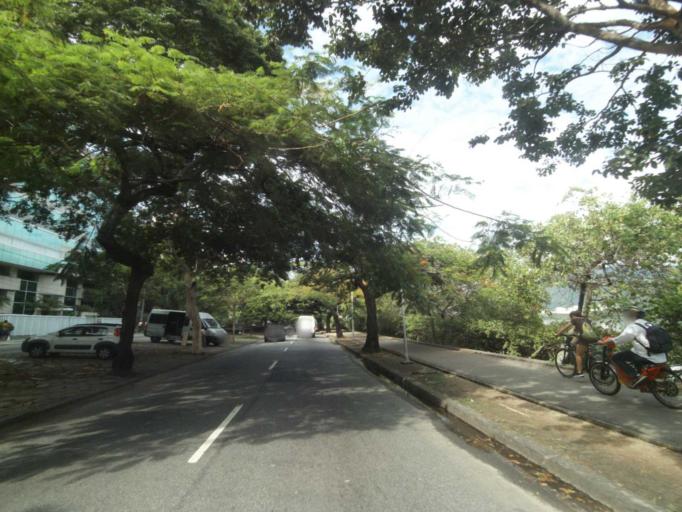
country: BR
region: Rio de Janeiro
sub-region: Rio De Janeiro
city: Rio de Janeiro
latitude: -22.9698
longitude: -43.2061
